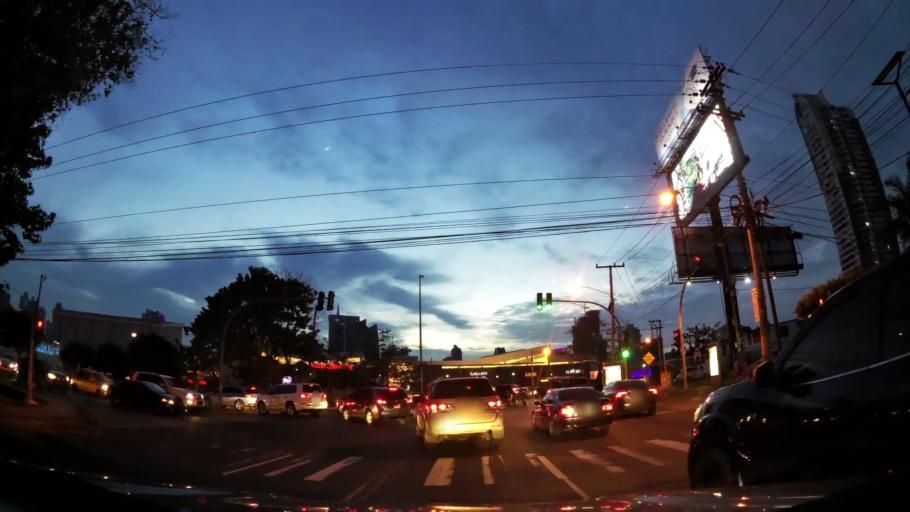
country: PA
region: Panama
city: Panama
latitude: 8.9870
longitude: -79.5094
